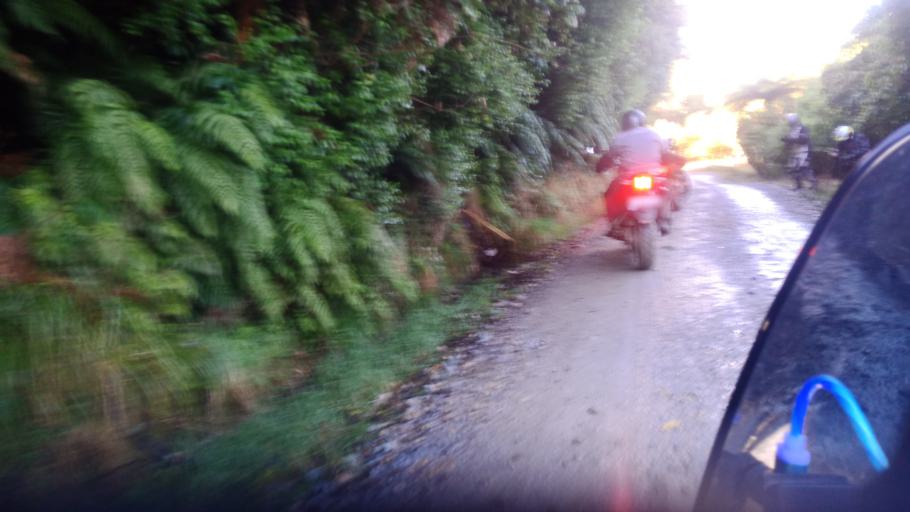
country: NZ
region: Hawke's Bay
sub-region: Wairoa District
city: Wairoa
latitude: -38.6669
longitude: 177.5289
